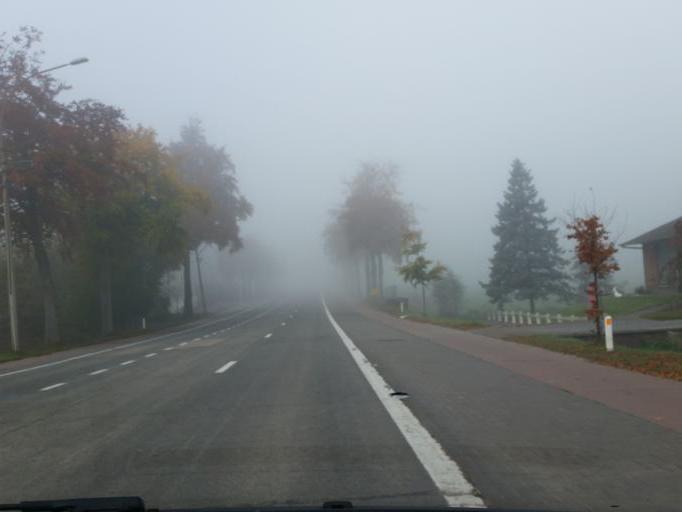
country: BE
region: Flanders
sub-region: Provincie Oost-Vlaanderen
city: Wetteren
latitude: 50.9728
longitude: 3.8686
